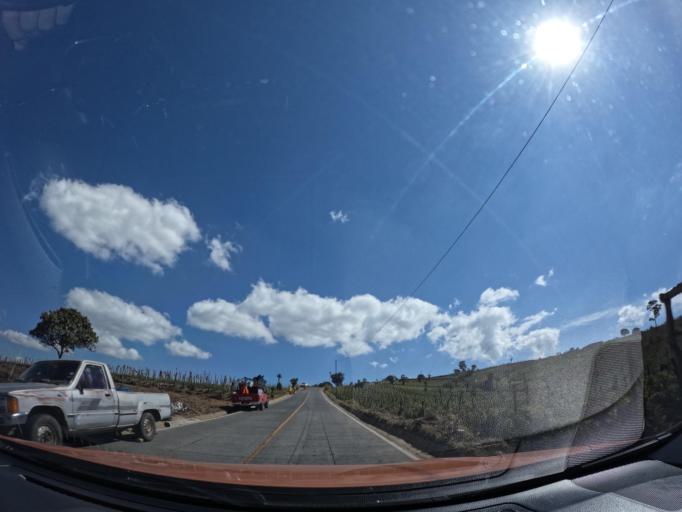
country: GT
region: Chimaltenango
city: Patzun
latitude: 14.6660
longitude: -91.0565
